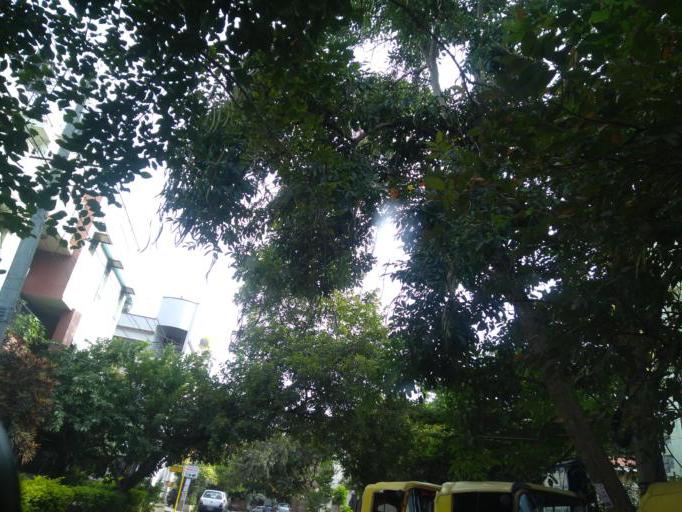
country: IN
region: Karnataka
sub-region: Bangalore Urban
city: Bangalore
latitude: 13.0049
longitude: 77.6583
